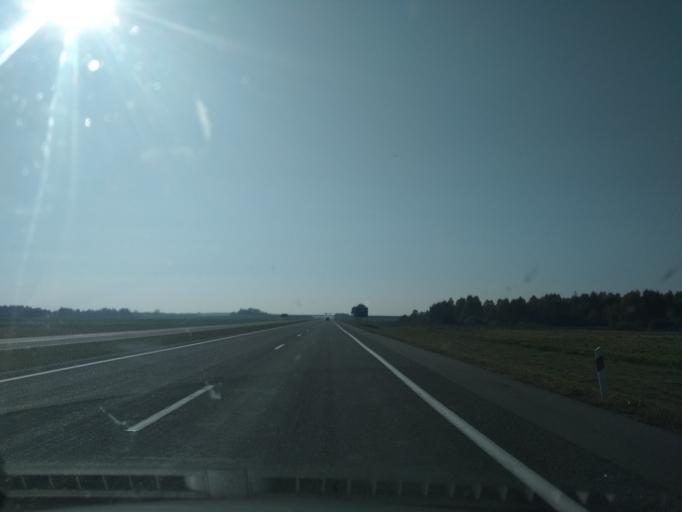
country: BY
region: Brest
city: Antopal'
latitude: 52.3152
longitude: 24.6089
